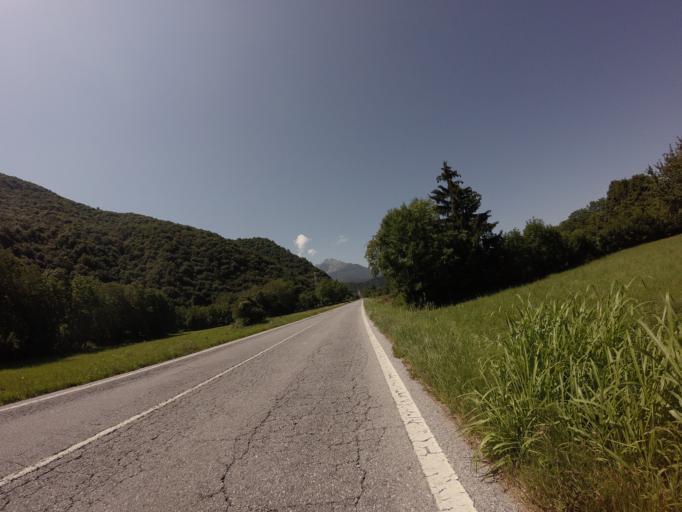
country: IT
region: Piedmont
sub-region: Provincia di Cuneo
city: Chiusa di Pesio
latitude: 44.3307
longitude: 7.6867
